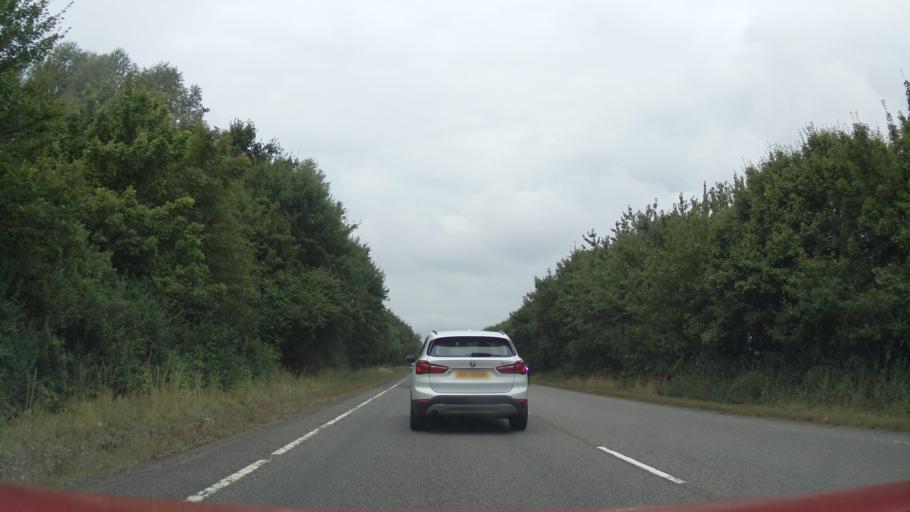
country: GB
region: England
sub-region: Nottinghamshire
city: South Collingham
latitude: 53.0907
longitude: -0.7637
